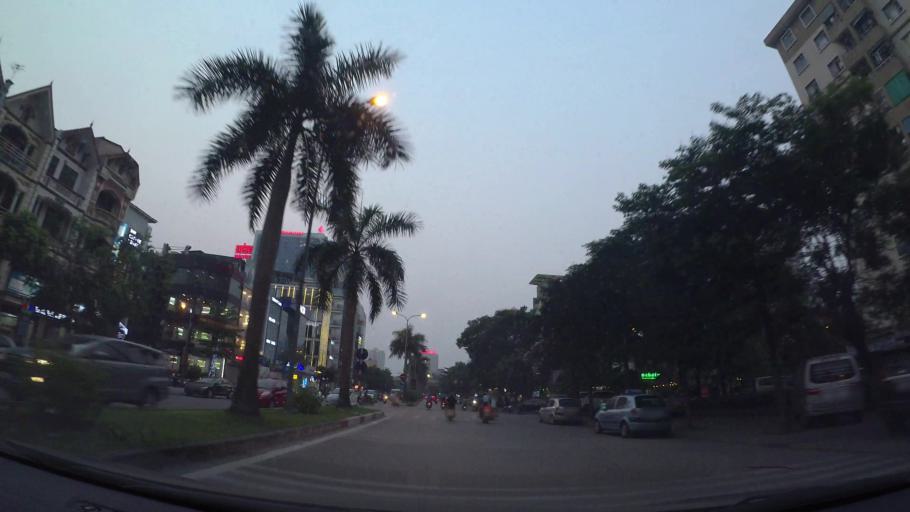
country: VN
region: Ha Noi
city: Ha Dong
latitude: 20.9773
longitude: 105.7880
